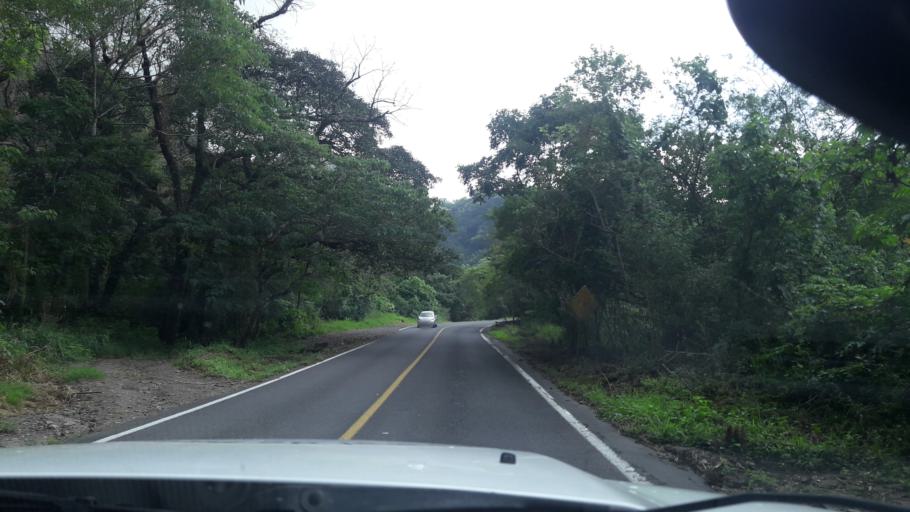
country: MX
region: Colima
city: Suchitlan
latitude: 19.4446
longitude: -103.7151
